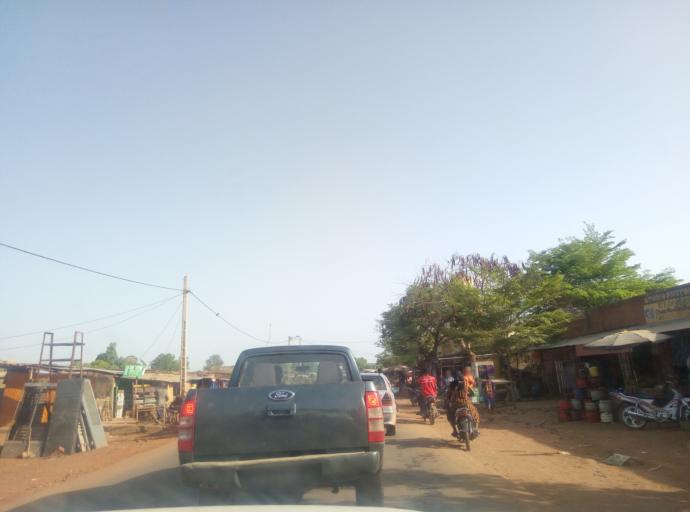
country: ML
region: Bamako
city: Bamako
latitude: 12.5885
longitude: -7.7665
